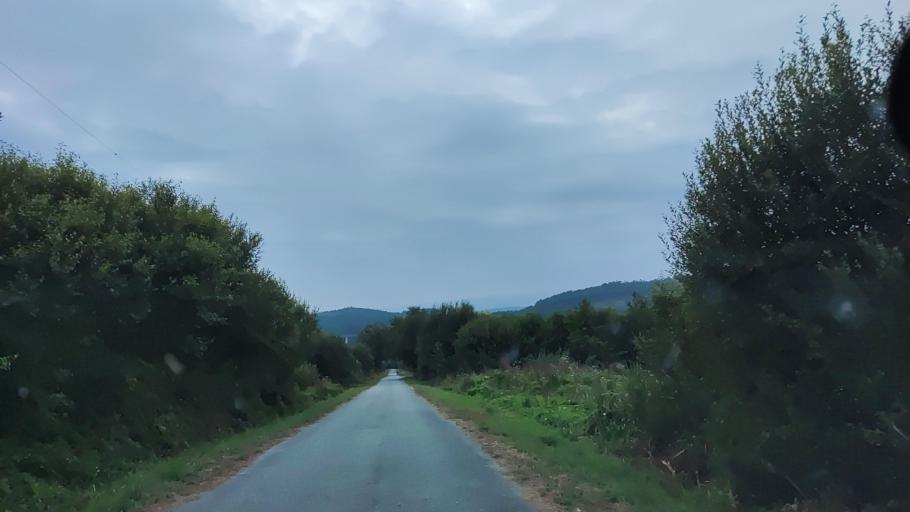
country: ES
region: Galicia
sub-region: Provincia da Coruna
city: Rois
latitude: 42.7149
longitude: -8.7085
